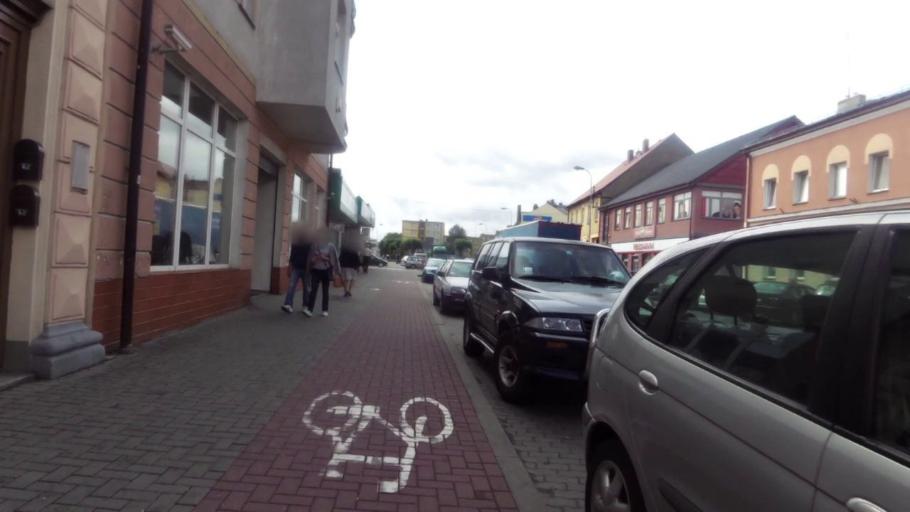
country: PL
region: West Pomeranian Voivodeship
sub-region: Powiat mysliborski
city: Debno
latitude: 52.7381
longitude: 14.6969
